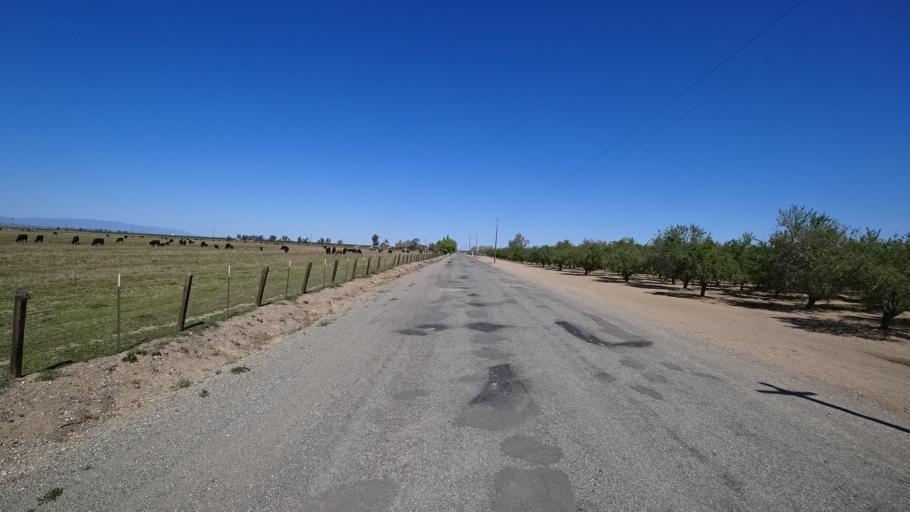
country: US
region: California
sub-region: Glenn County
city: Willows
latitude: 39.6284
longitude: -122.2348
